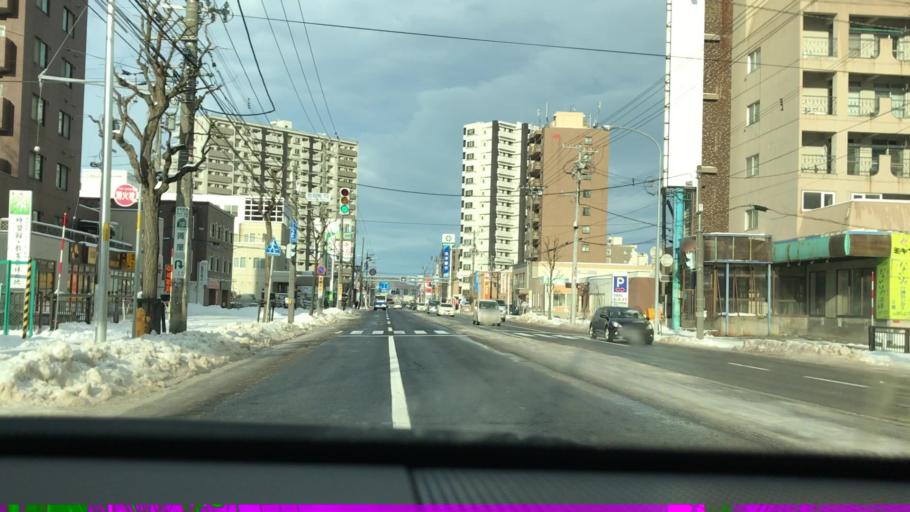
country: JP
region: Hokkaido
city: Sapporo
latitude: 43.0859
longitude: 141.2772
